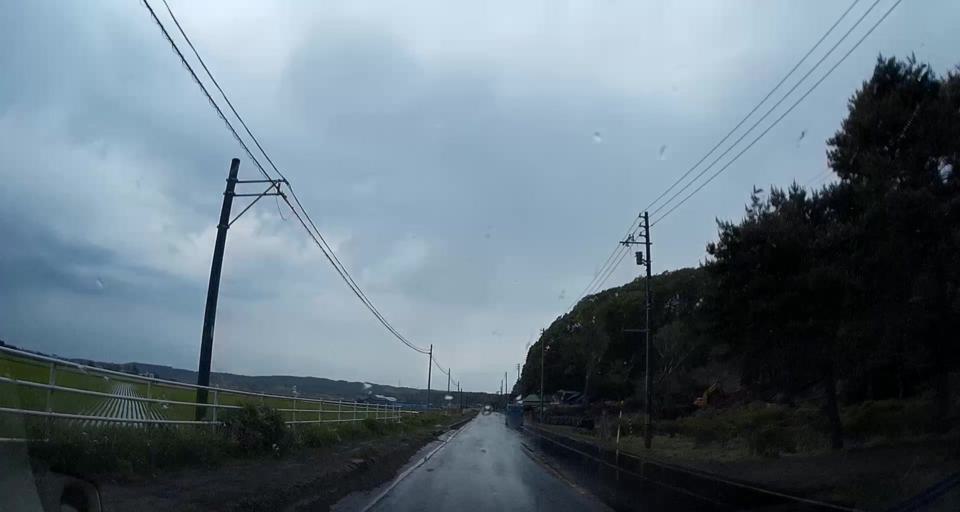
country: JP
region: Hokkaido
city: Chitose
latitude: 42.7359
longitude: 141.8982
